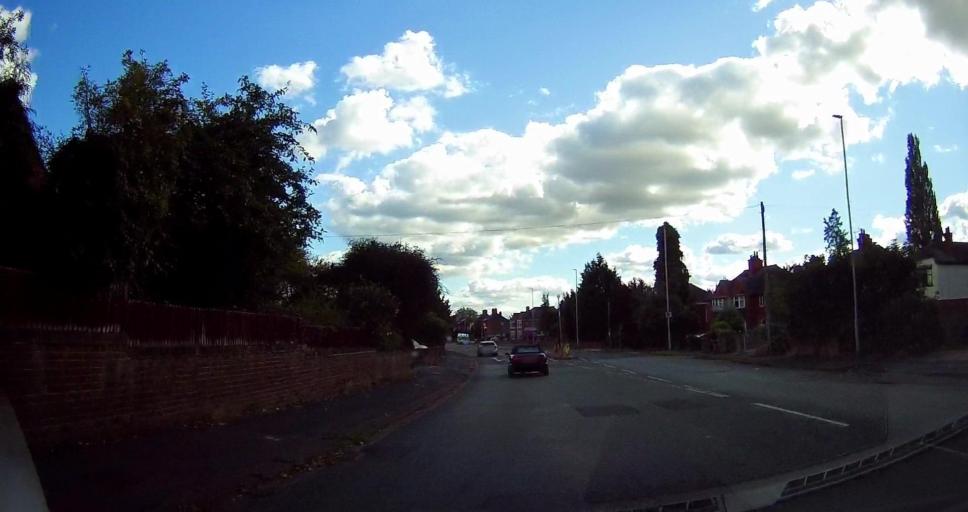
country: GB
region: England
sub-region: Staffordshire
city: Stafford
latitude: 52.8255
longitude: -2.1290
